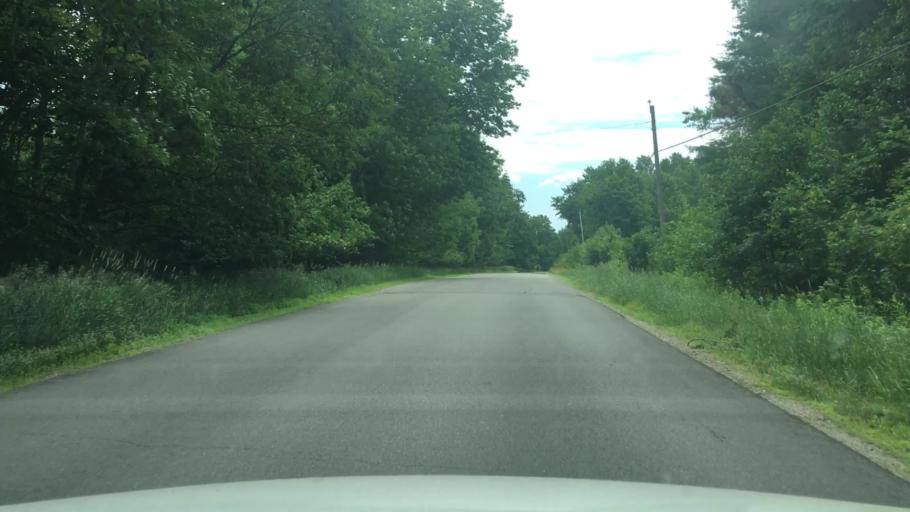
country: US
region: Maine
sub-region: Waldo County
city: Searsmont
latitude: 44.4513
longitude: -69.2515
